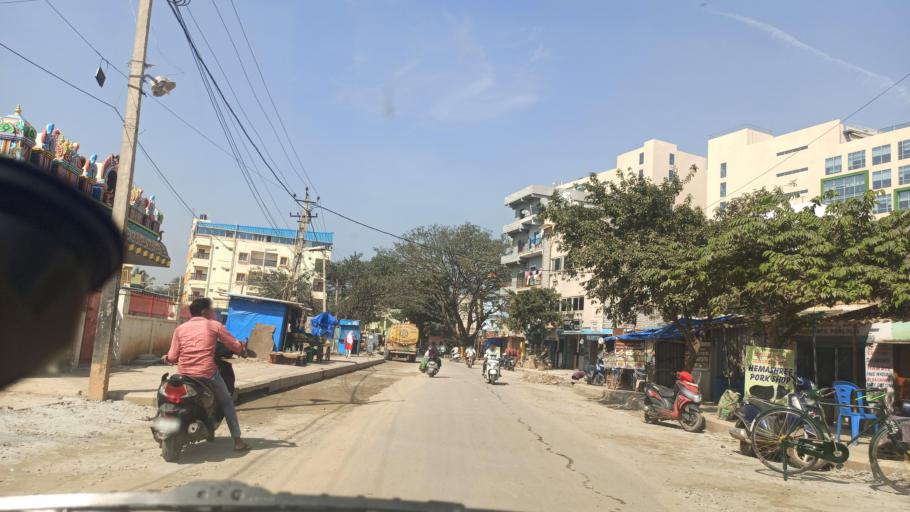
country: IN
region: Karnataka
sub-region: Bangalore Urban
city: Bangalore
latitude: 12.9257
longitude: 77.6927
